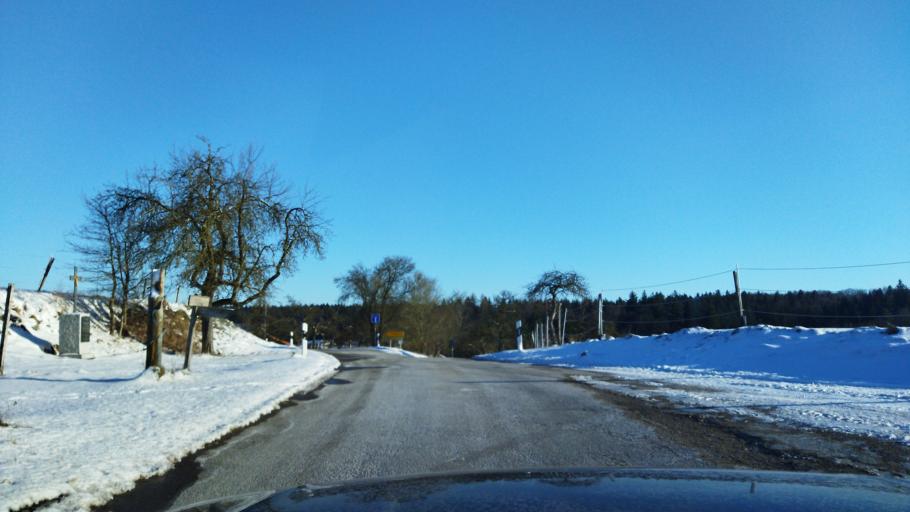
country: DE
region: Baden-Wuerttemberg
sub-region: Regierungsbezirk Stuttgart
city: Gerabronn
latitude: 48.9718
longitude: 9.9168
